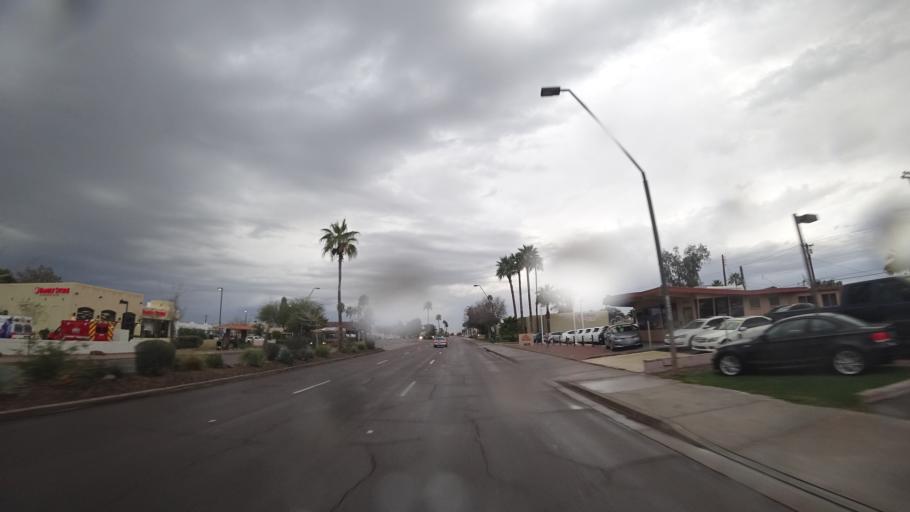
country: US
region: Arizona
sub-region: Maricopa County
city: Tempe
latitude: 33.4538
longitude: -111.9263
